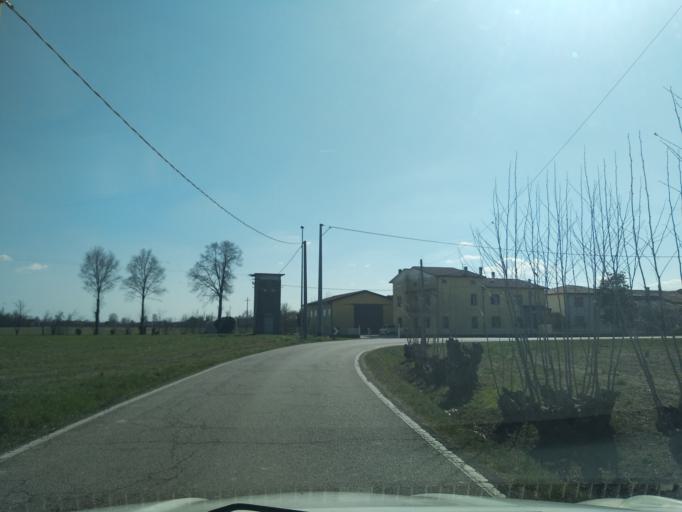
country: IT
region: Veneto
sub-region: Provincia di Padova
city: Villafranca Padovana
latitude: 45.4982
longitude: 11.8094
